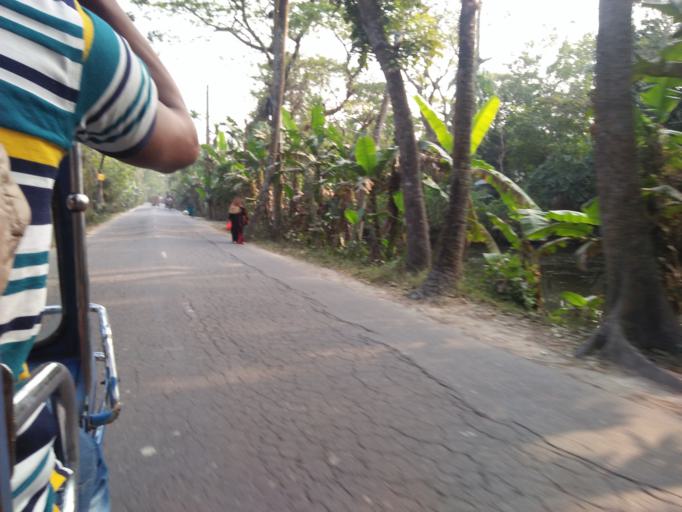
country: BD
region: Barisal
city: Bhola
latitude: 22.7001
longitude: 90.6420
